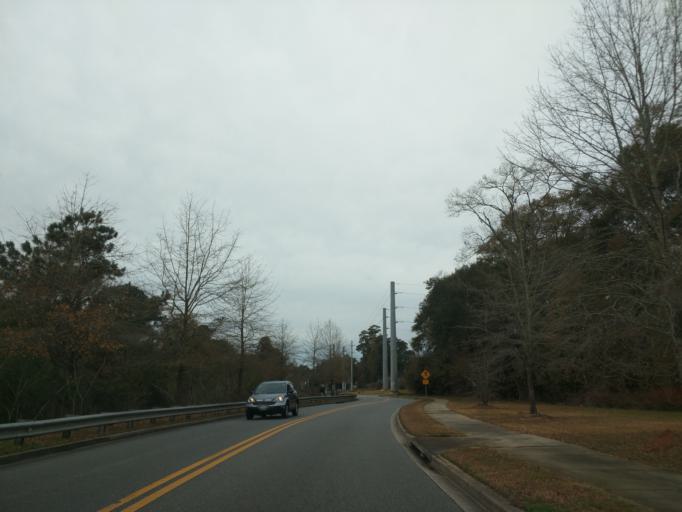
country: US
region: Florida
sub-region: Leon County
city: Tallahassee
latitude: 30.4597
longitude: -84.2183
